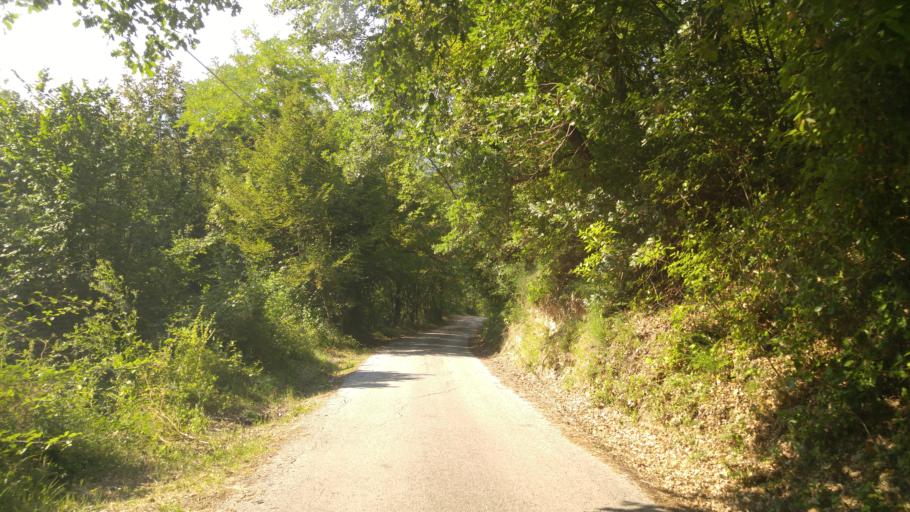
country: IT
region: The Marches
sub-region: Provincia di Pesaro e Urbino
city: Fossombrone
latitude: 43.6775
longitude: 12.8055
